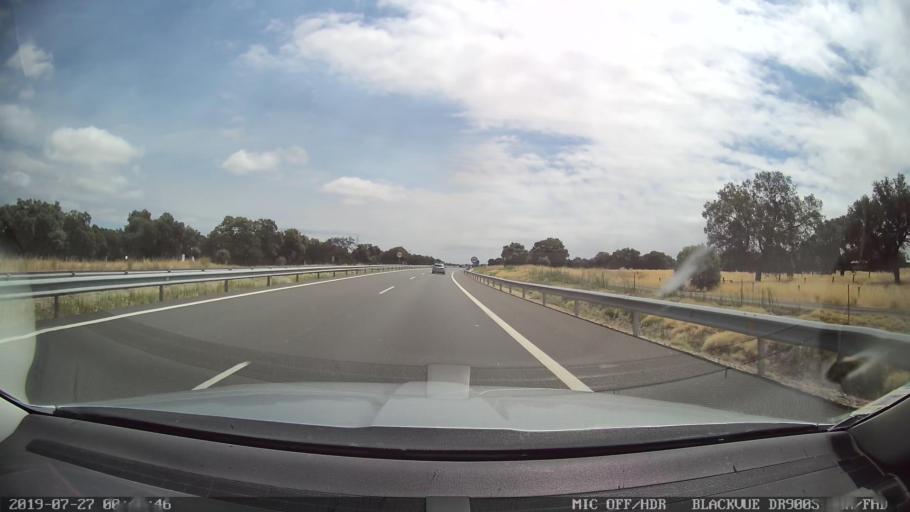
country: ES
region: Castille-La Mancha
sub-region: Province of Toledo
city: Alcanizo
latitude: 39.9249
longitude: -5.1116
